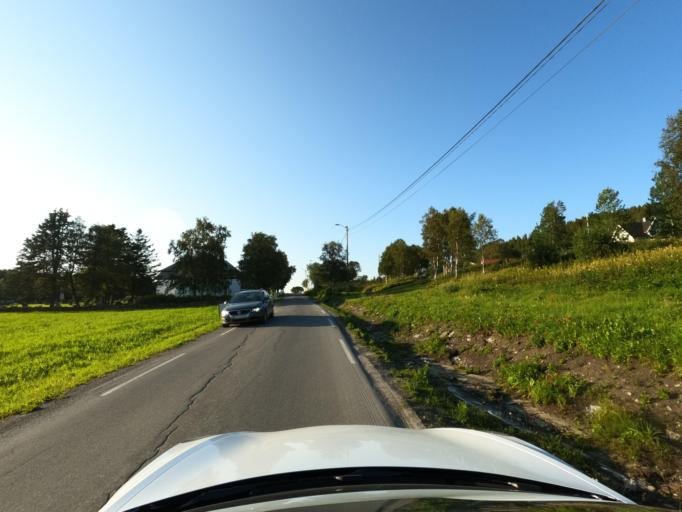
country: NO
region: Nordland
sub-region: Ballangen
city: Ballangen
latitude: 68.4591
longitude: 16.6996
